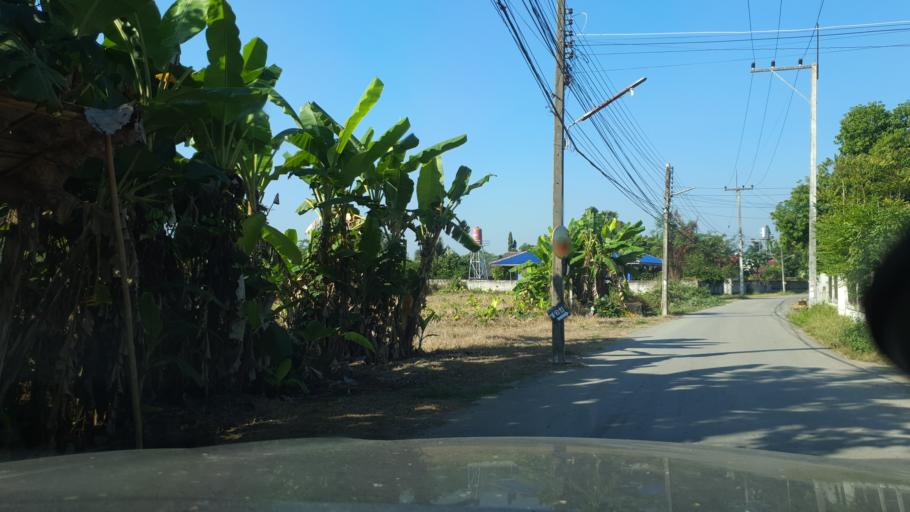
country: TH
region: Chiang Mai
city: San Kamphaeng
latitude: 18.7505
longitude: 99.1679
